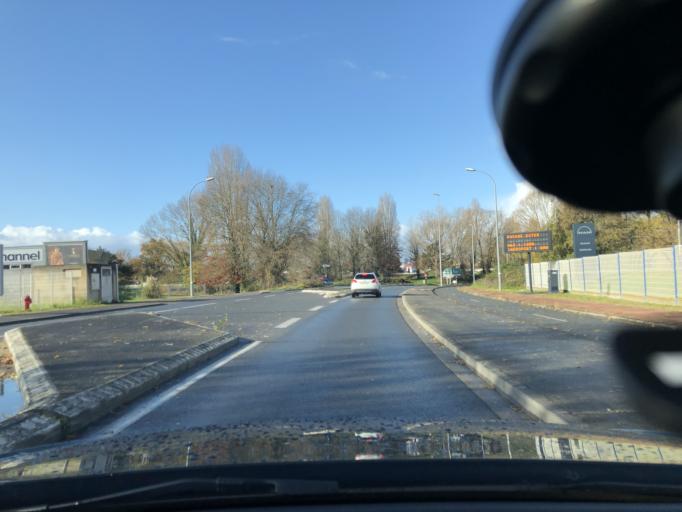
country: FR
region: Aquitaine
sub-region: Departement de la Gironde
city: Bruges
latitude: 44.8874
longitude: -0.5983
